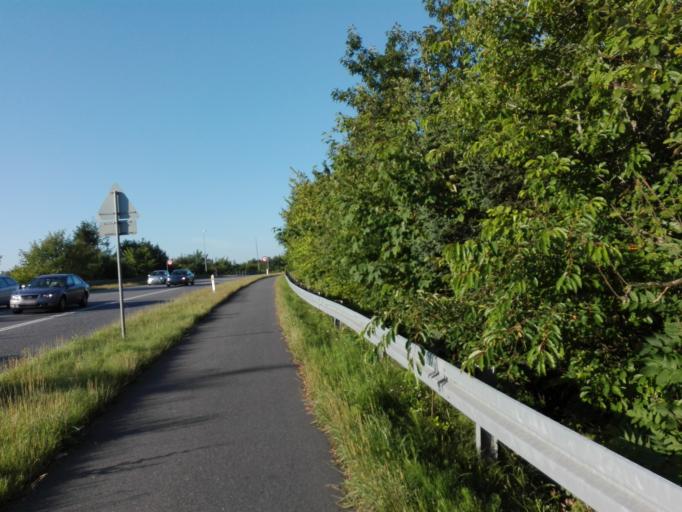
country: DK
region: Central Jutland
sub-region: Arhus Kommune
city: Tranbjerg
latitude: 56.0963
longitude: 10.1390
